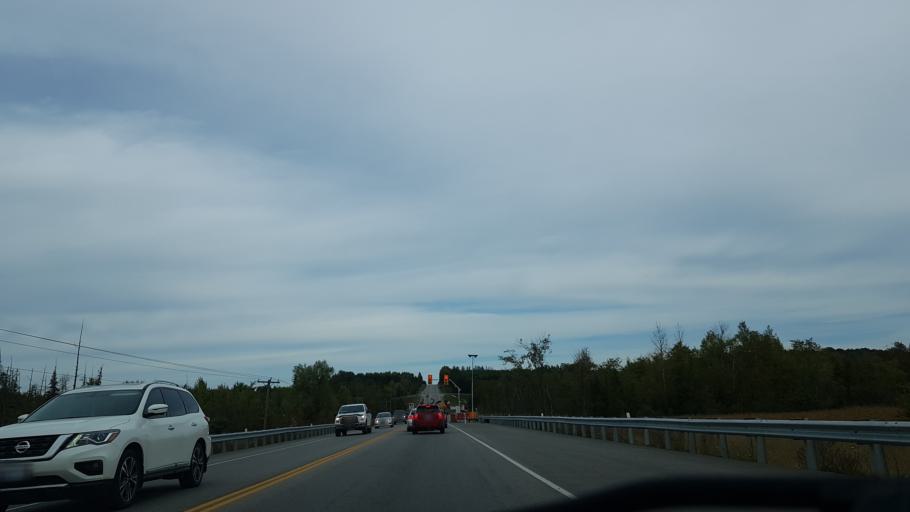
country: CA
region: Ontario
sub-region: Wellington County
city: Guelph
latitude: 43.7037
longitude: -80.1278
